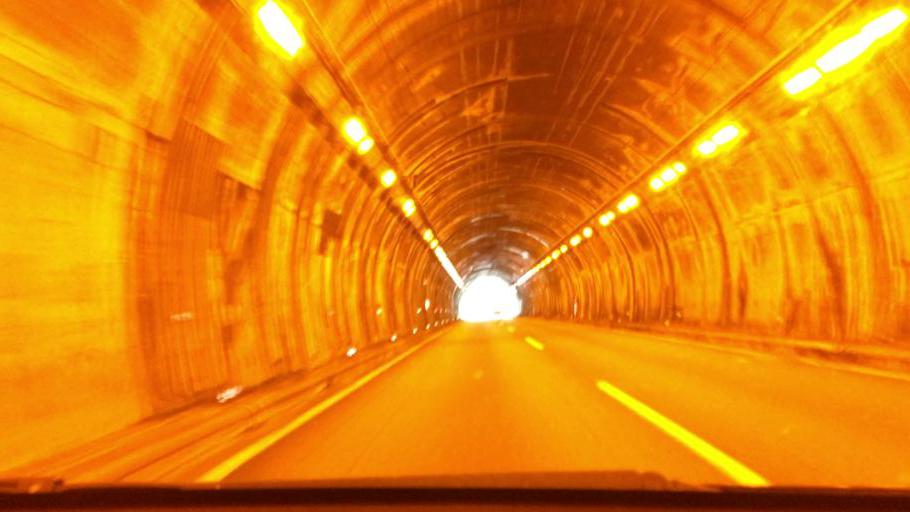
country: JP
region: Yamaguchi
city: Ogori-shimogo
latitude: 34.1392
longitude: 131.3613
